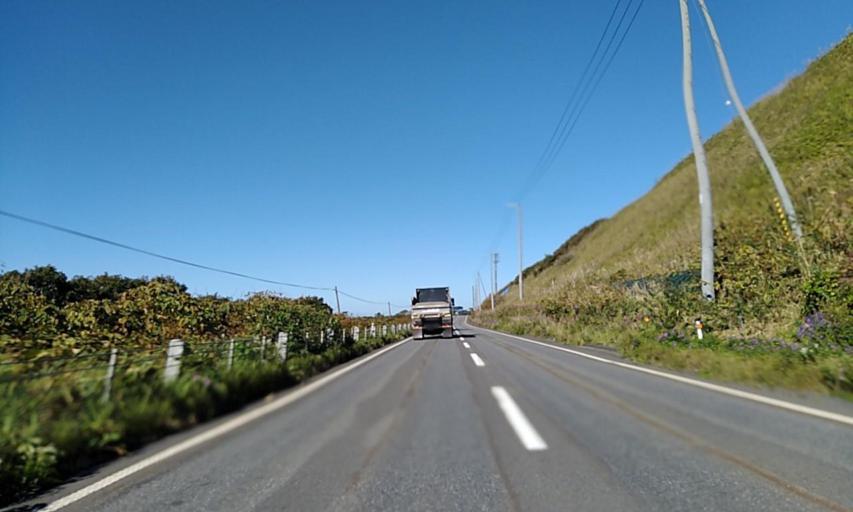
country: JP
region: Hokkaido
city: Shizunai-furukawacho
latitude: 42.4684
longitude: 142.1335
